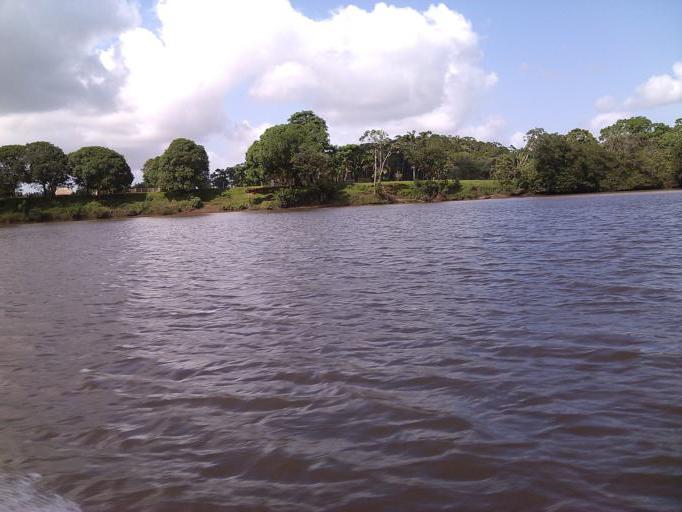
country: NI
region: Atlantico Sur
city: Rama
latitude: 12.1190
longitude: -84.0724
